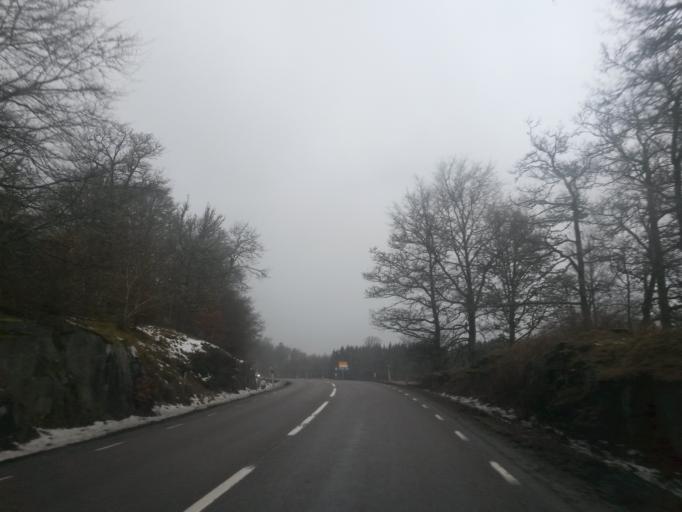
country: SE
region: Vaestra Goetaland
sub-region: Alingsas Kommun
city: Sollebrunn
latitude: 58.1624
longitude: 12.4243
